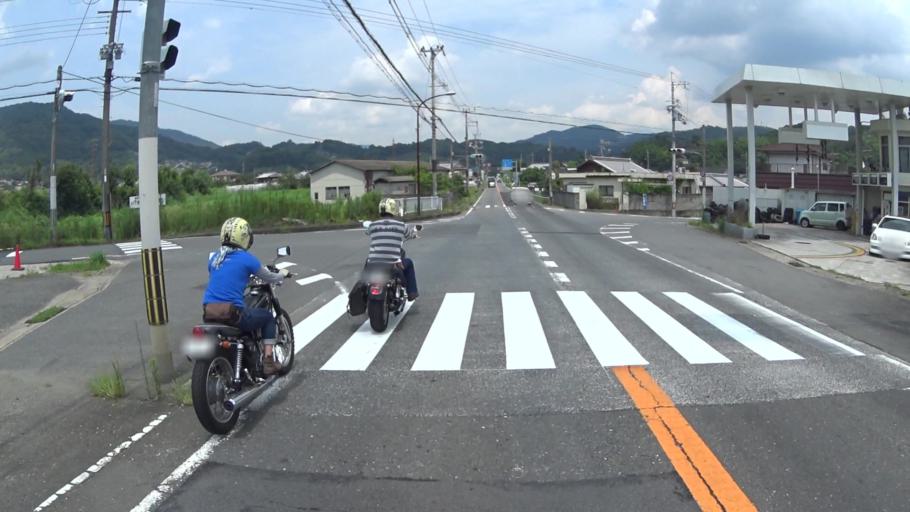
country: JP
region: Nara
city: Nara-shi
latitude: 34.7650
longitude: 135.8656
